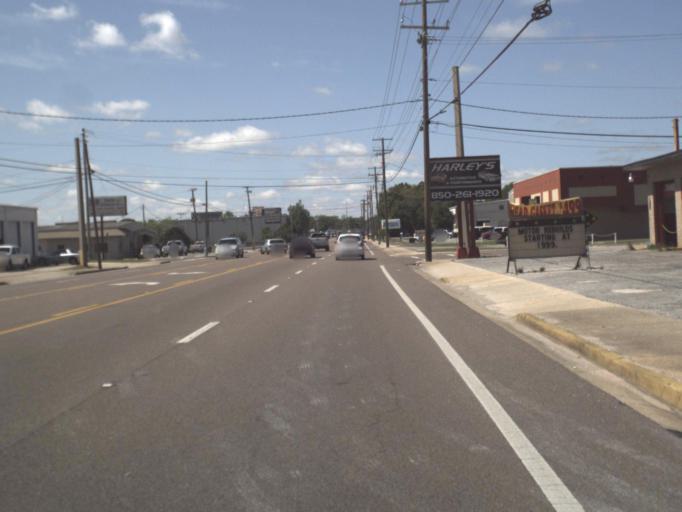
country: US
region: Florida
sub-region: Escambia County
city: Brent
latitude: 30.4552
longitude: -87.2360
